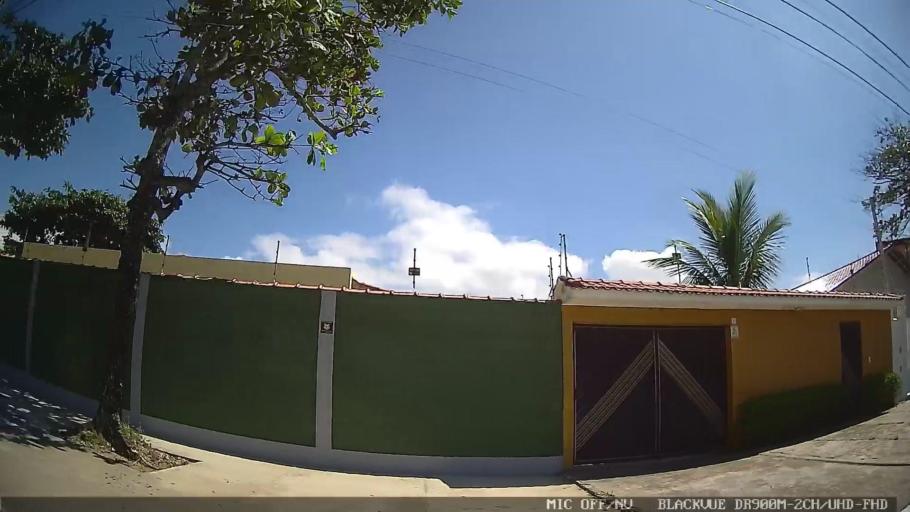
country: BR
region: Sao Paulo
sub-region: Peruibe
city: Peruibe
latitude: -24.3213
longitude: -46.9922
